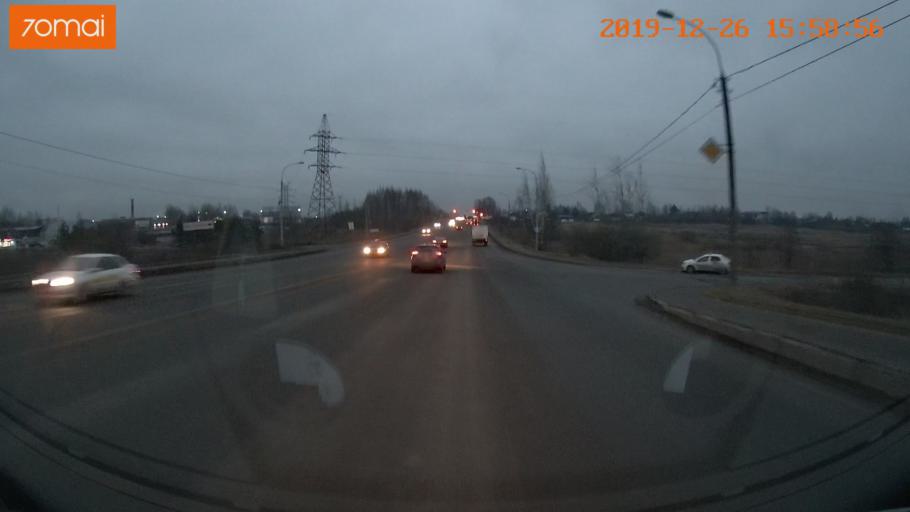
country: RU
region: Jaroslavl
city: Rybinsk
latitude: 58.0353
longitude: 38.8001
